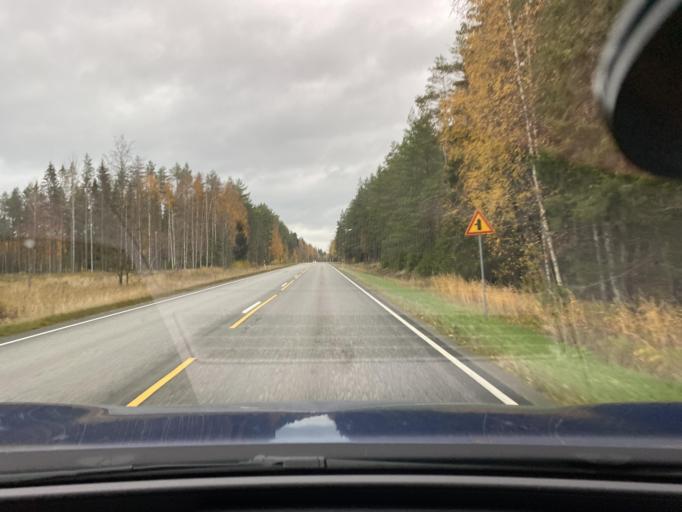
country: FI
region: Varsinais-Suomi
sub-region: Loimaa
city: Ylaene
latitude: 60.8971
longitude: 22.4059
